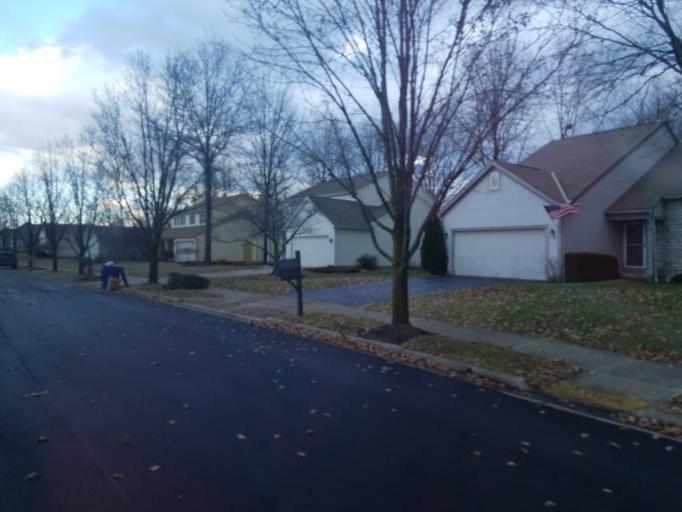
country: US
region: Ohio
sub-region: Delaware County
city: Delaware
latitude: 40.3160
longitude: -83.1003
